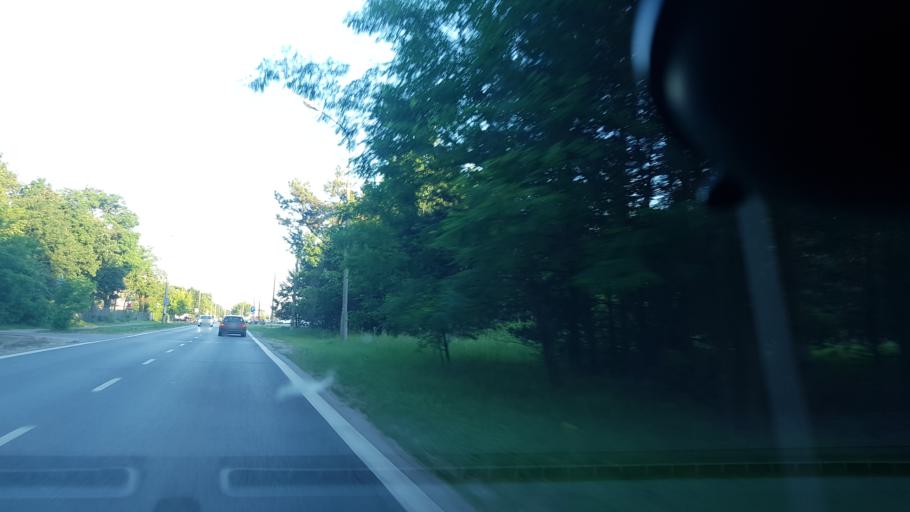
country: PL
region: Masovian Voivodeship
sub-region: Warszawa
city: Wawer
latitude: 52.1754
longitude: 21.1980
